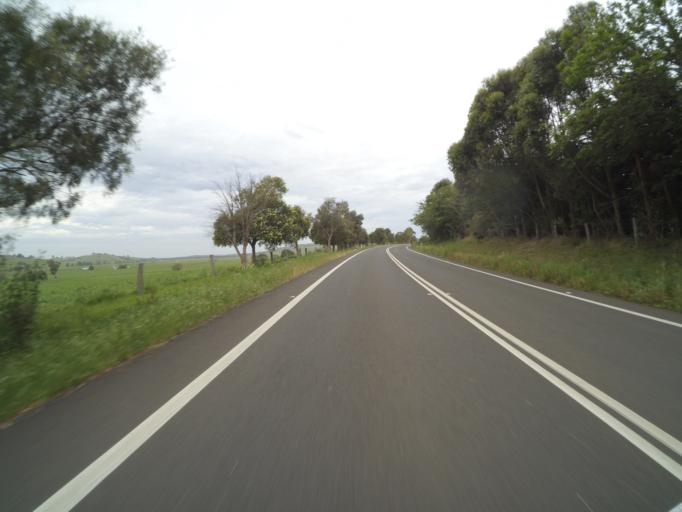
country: AU
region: New South Wales
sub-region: Kiama
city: Jamberoo
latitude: -34.6517
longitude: 150.8010
